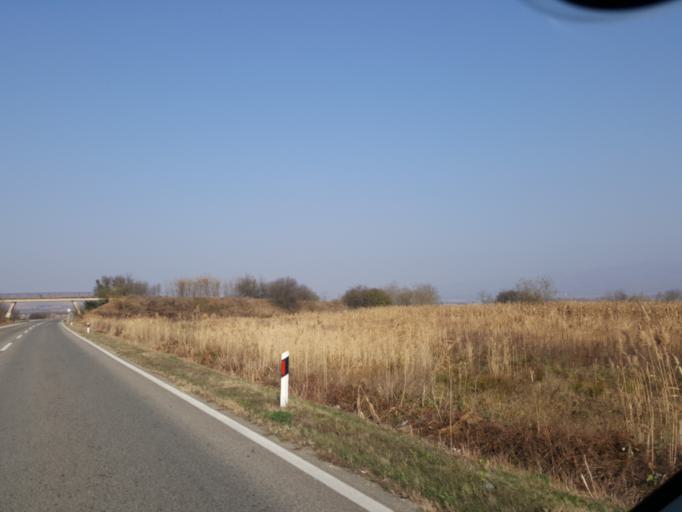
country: RS
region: Central Serbia
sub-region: Jablanicki Okrug
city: Leskovac
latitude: 43.0320
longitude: 21.9421
